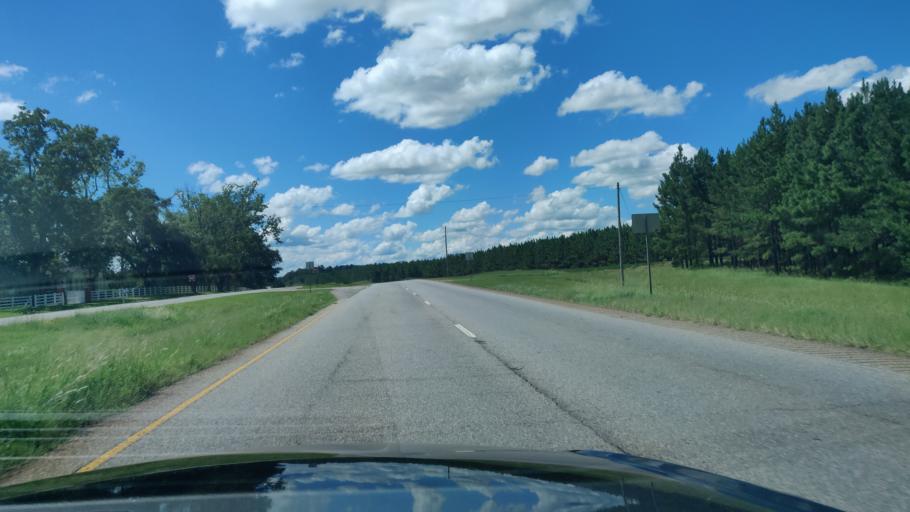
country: US
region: Georgia
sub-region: Stewart County
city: Richland
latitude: 32.0200
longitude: -84.6637
